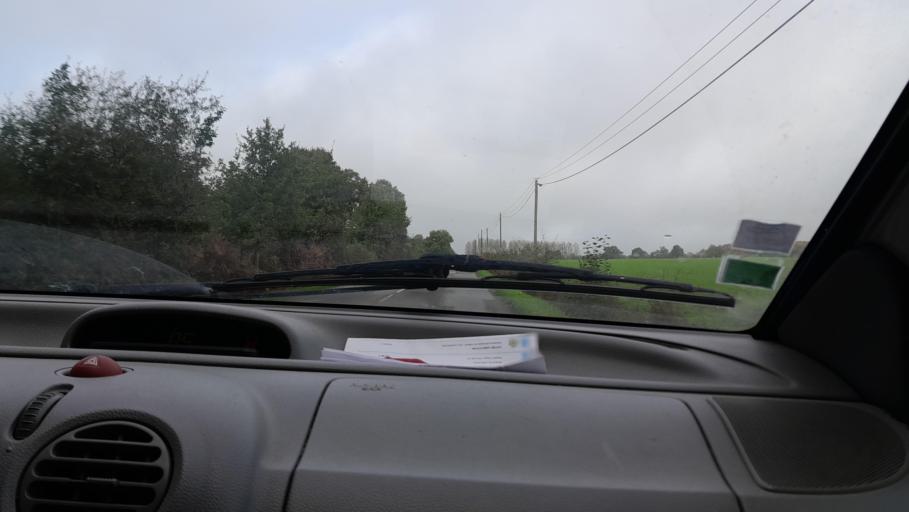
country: FR
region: Brittany
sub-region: Departement d'Ille-et-Vilaine
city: Luitre
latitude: 48.2275
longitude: -1.0996
